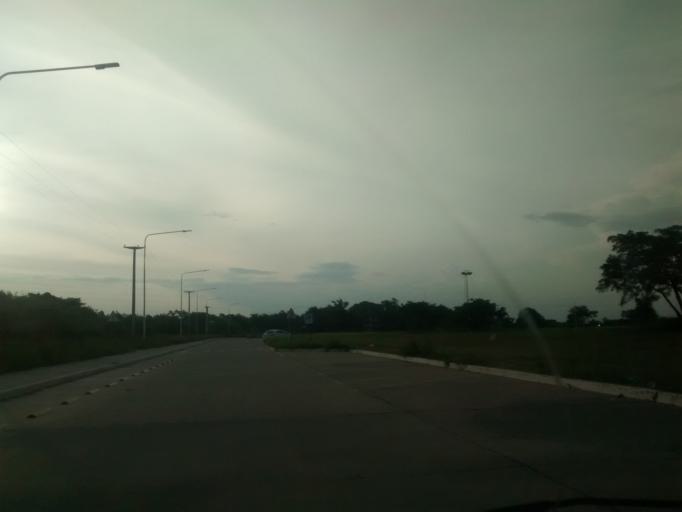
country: AR
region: Chaco
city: Resistencia
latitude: -27.4333
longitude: -58.9710
